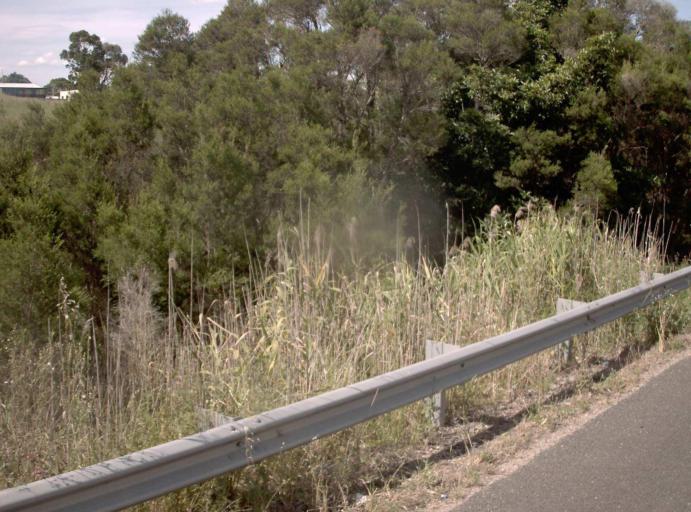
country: AU
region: Victoria
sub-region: East Gippsland
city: Bairnsdale
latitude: -37.8181
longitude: 147.7341
